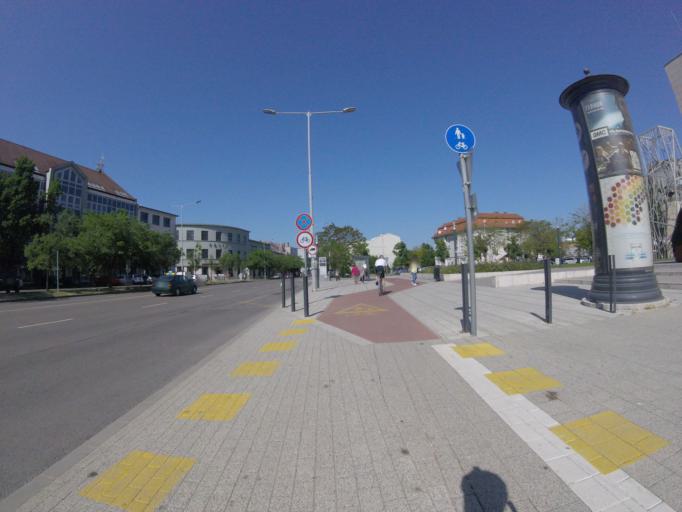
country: HU
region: Jasz-Nagykun-Szolnok
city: Szolnok
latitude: 47.1778
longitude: 20.1847
